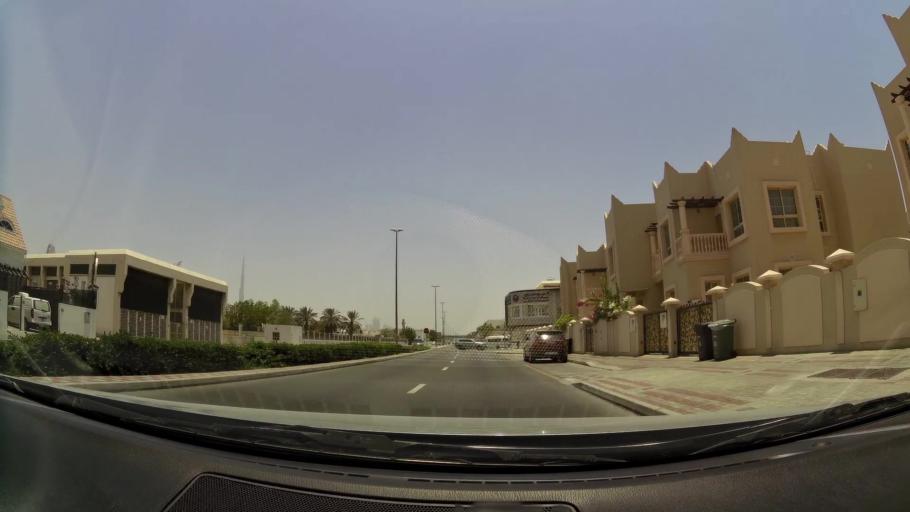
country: AE
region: Ash Shariqah
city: Sharjah
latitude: 25.2359
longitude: 55.2710
